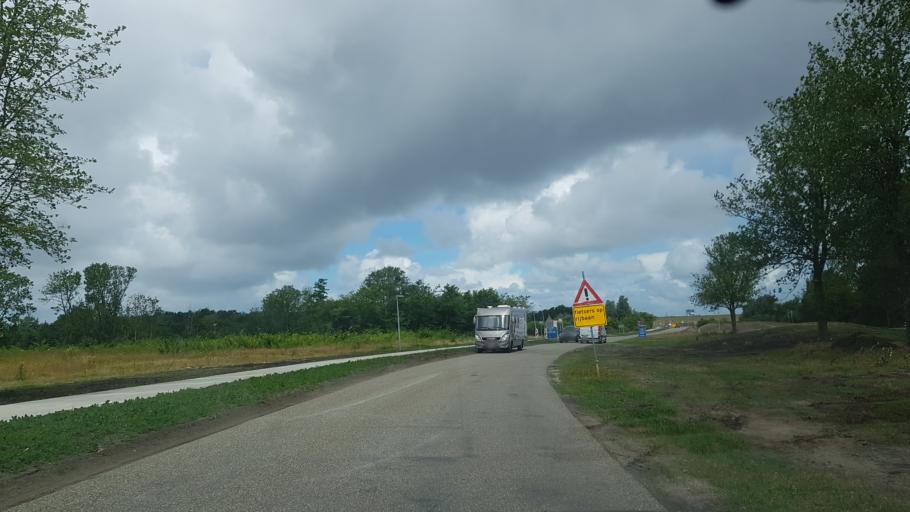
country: NL
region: Friesland
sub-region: Gemeente Dongeradeel
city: Anjum
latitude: 53.4042
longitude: 6.2129
